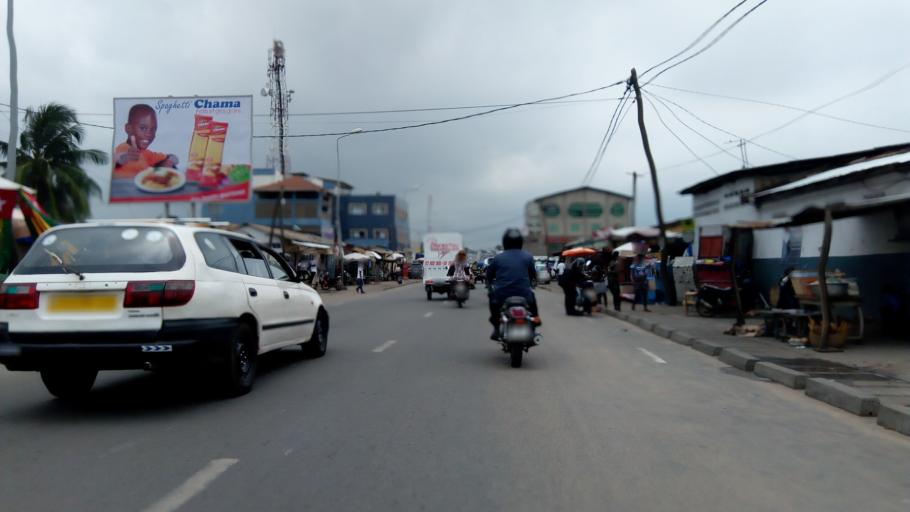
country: TG
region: Maritime
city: Lome
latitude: 6.1418
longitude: 1.2297
